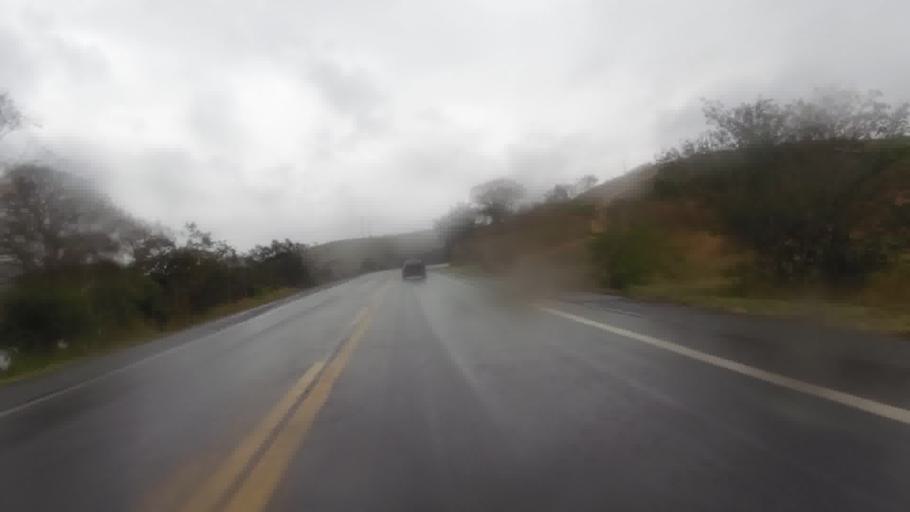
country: BR
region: Espirito Santo
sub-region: Cachoeiro De Itapemirim
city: Cachoeiro de Itapemirim
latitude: -20.9060
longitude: -41.0654
